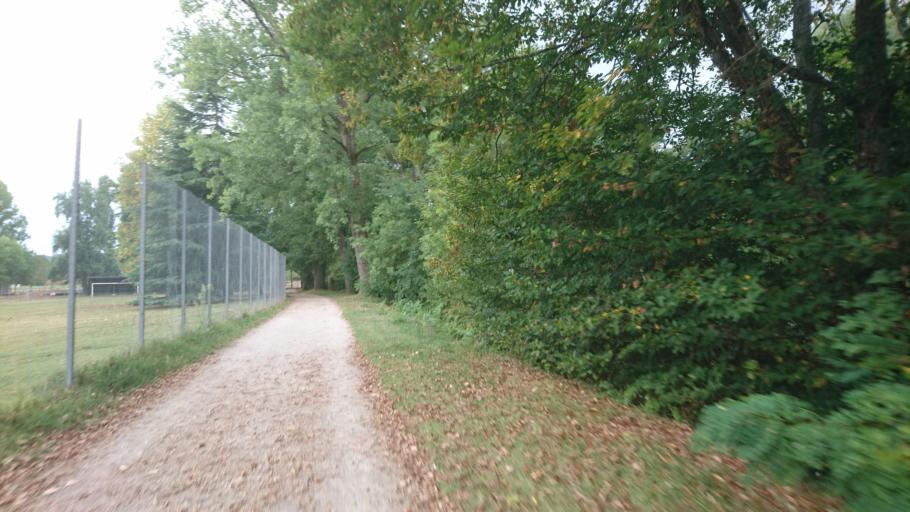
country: FR
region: Limousin
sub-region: Departement de la Correze
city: Ussac
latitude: 45.1599
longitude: 1.4901
